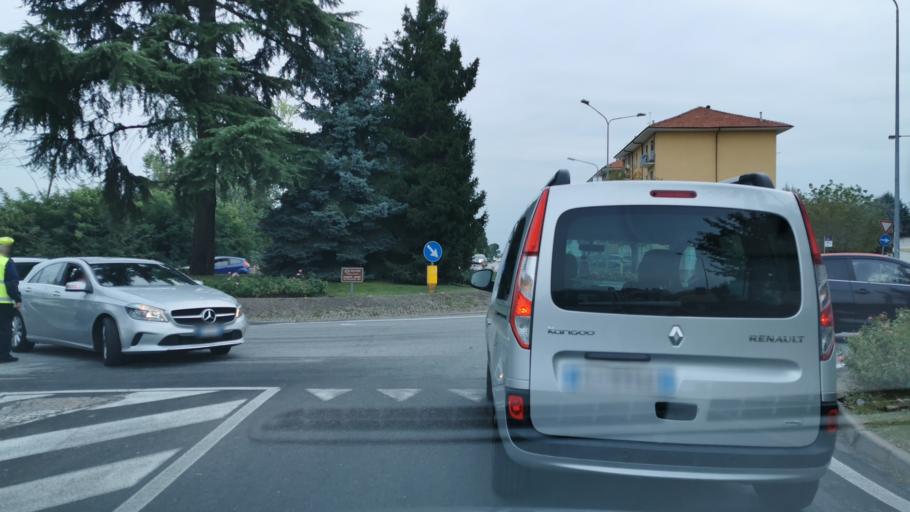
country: IT
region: Piedmont
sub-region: Provincia di Cuneo
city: Bra
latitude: 44.6846
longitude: 7.8500
